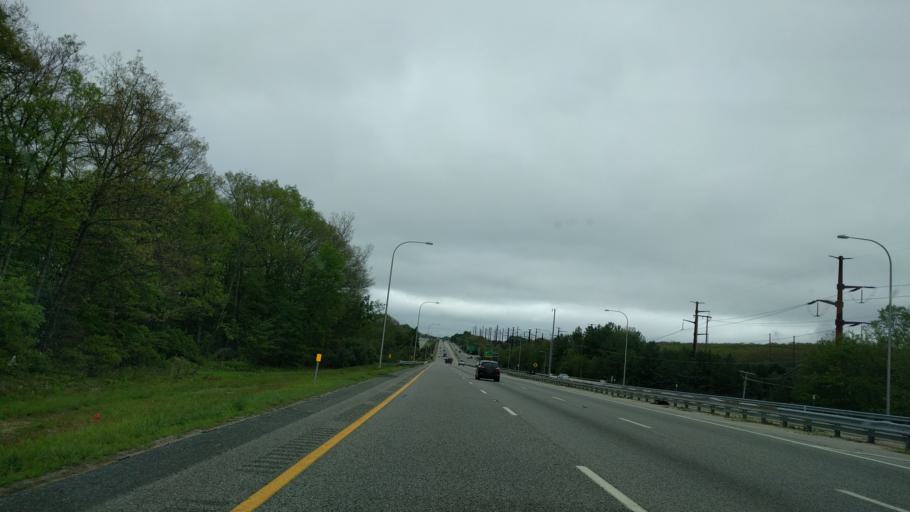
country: US
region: Rhode Island
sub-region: Providence County
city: Johnston
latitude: 41.8305
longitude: -71.5180
